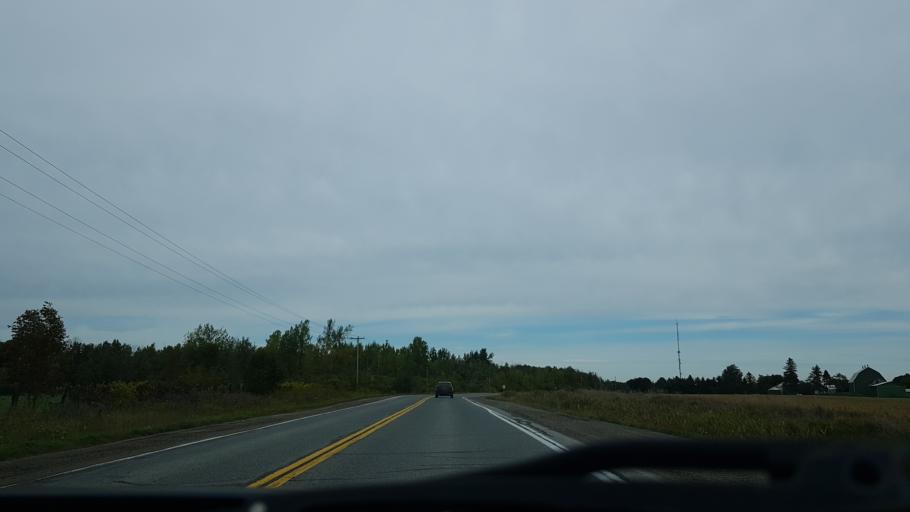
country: CA
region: Ontario
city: Orangeville
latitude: 43.9026
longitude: -79.9485
